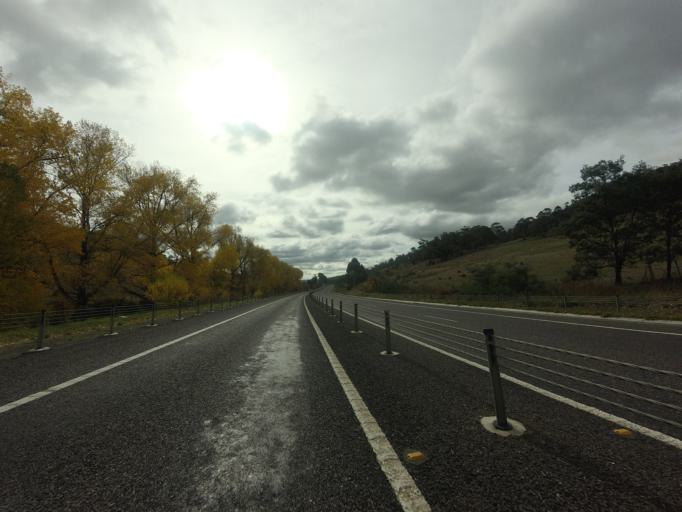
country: AU
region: Tasmania
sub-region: Brighton
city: Bridgewater
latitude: -42.5624
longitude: 147.2084
